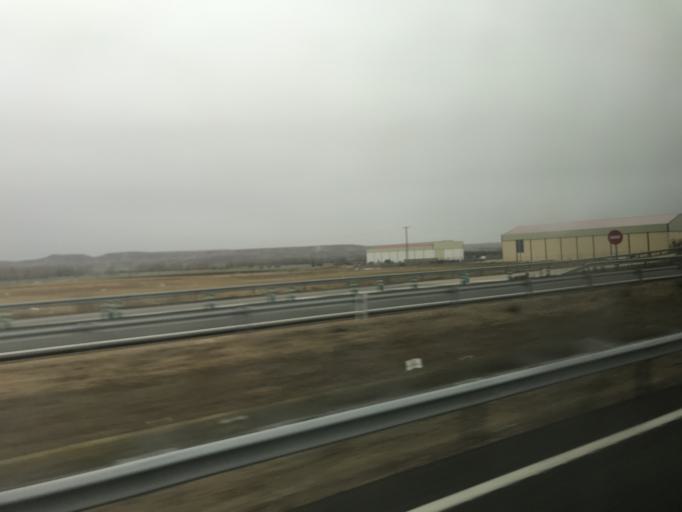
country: ES
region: Castille and Leon
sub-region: Provincia de Burgos
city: Villazopeque
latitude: 42.2048
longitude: -4.0164
